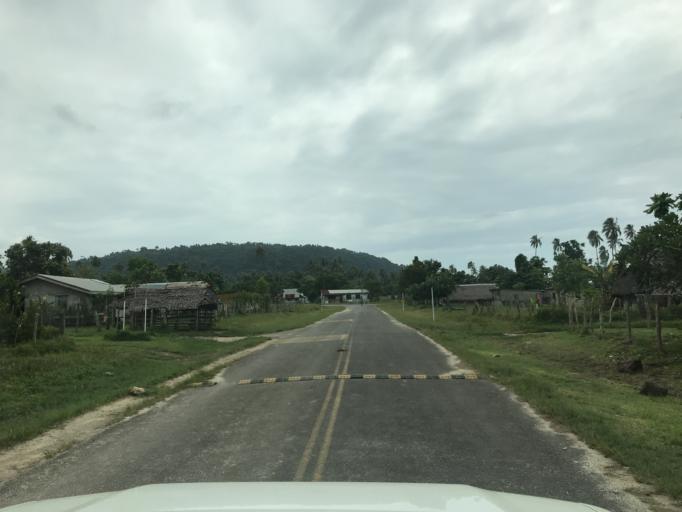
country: VU
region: Sanma
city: Port-Olry
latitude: -15.0434
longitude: 167.0721
